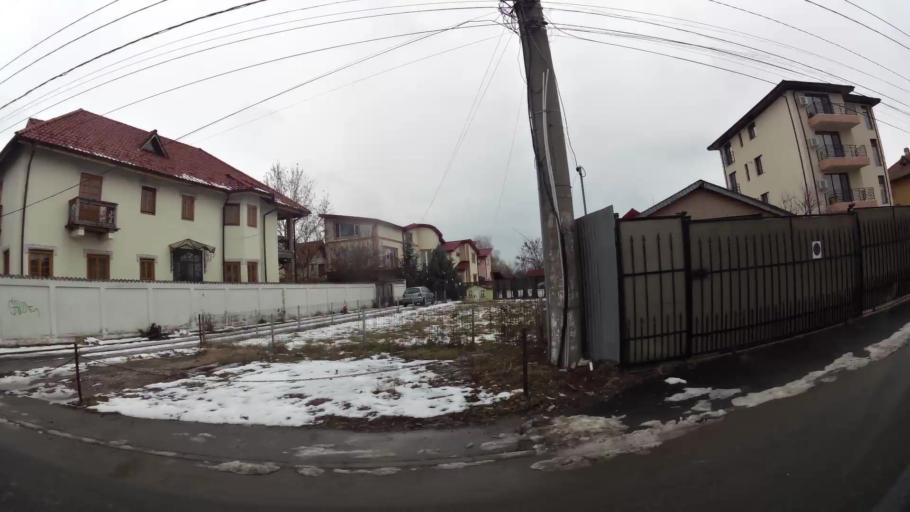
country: RO
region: Ilfov
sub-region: Comuna Otopeni
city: Otopeni
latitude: 44.5546
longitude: 26.0783
